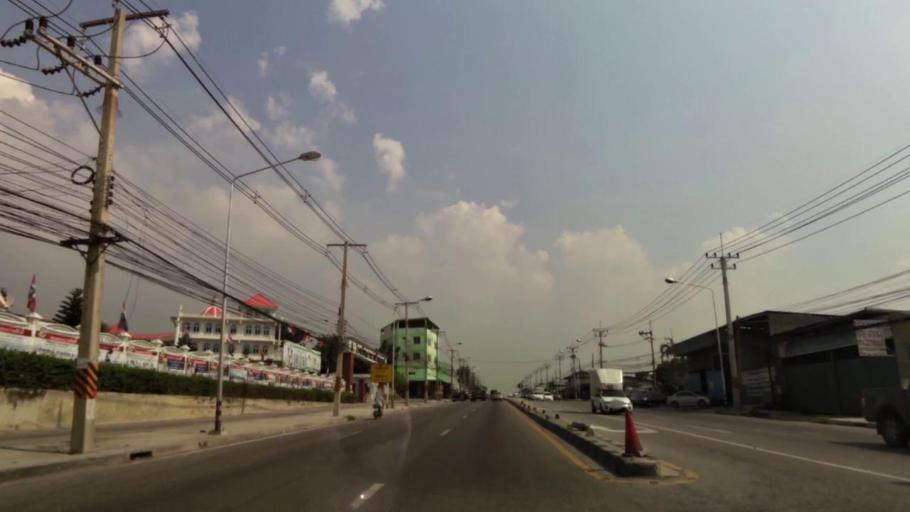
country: TH
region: Chon Buri
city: Chon Buri
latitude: 13.3482
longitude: 101.0188
